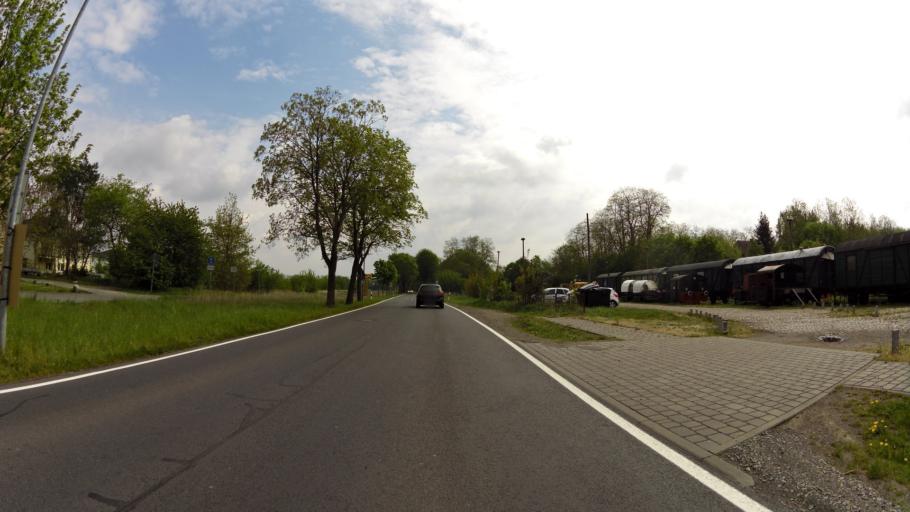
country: DE
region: Brandenburg
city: Mittenwalde
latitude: 52.2597
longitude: 13.5500
